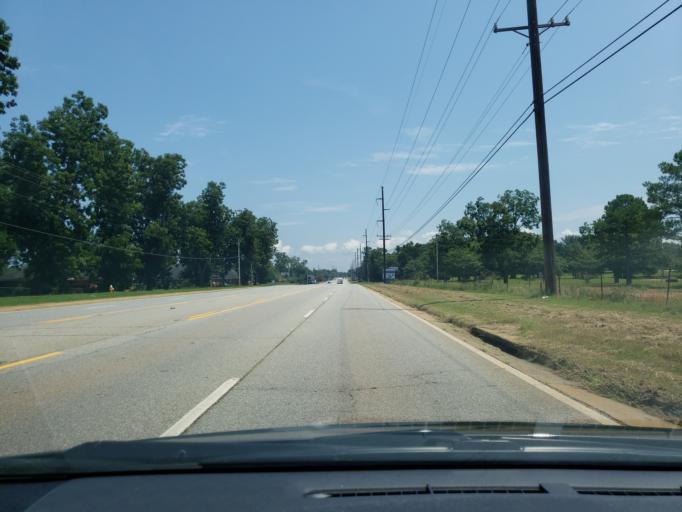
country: US
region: Georgia
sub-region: Dougherty County
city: Albany
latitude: 31.5856
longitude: -84.2293
